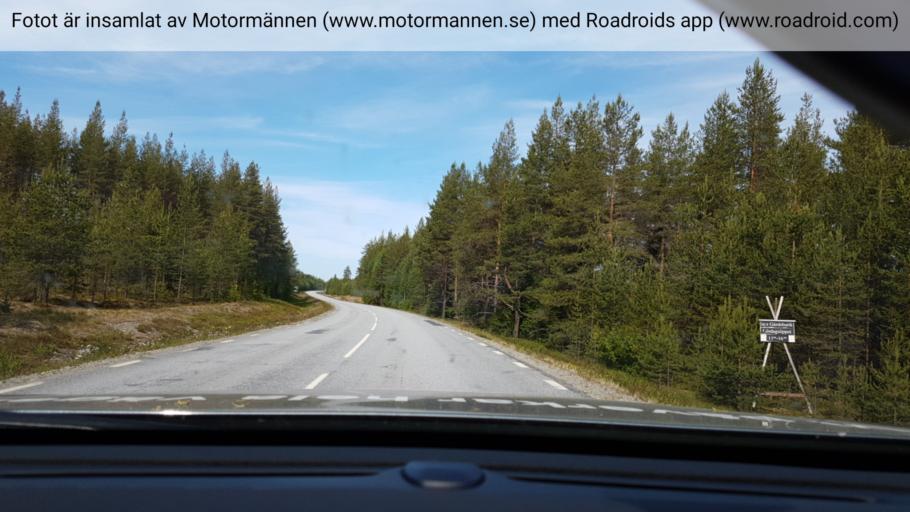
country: SE
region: Vaesterbotten
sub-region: Asele Kommun
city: Asele
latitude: 64.2066
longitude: 17.0087
